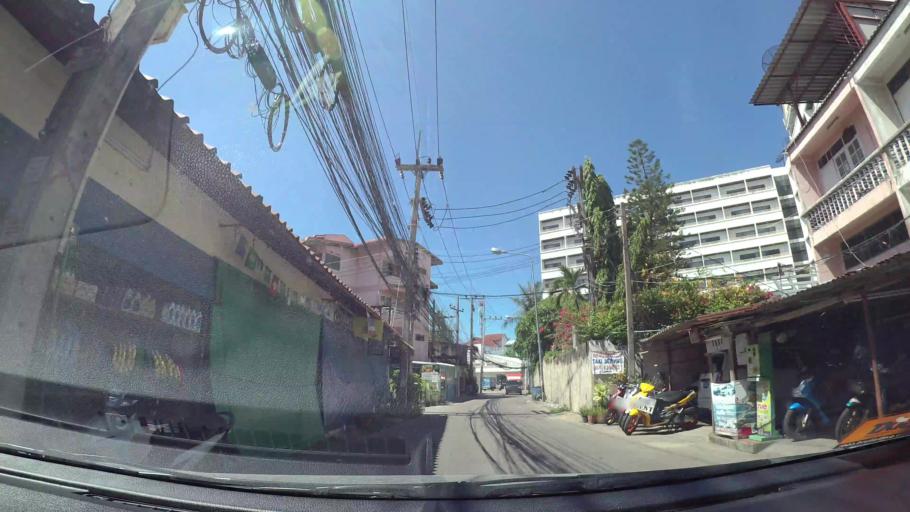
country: TH
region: Chon Buri
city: Phatthaya
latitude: 12.9363
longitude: 100.8905
